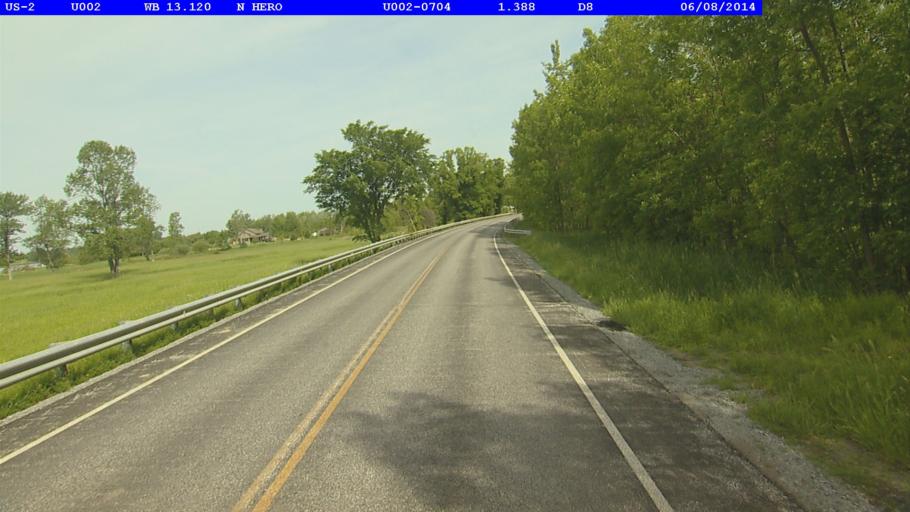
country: US
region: Vermont
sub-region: Grand Isle County
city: North Hero
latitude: 44.8670
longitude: -73.2680
